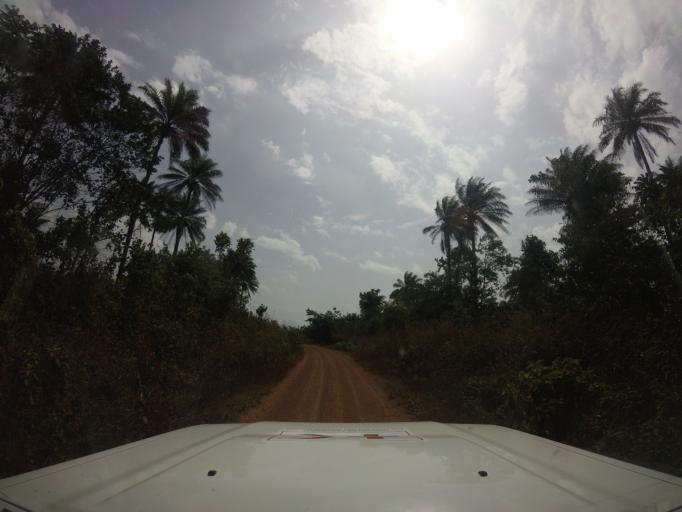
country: LR
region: Grand Cape Mount
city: Robertsport
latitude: 6.9311
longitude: -11.3503
